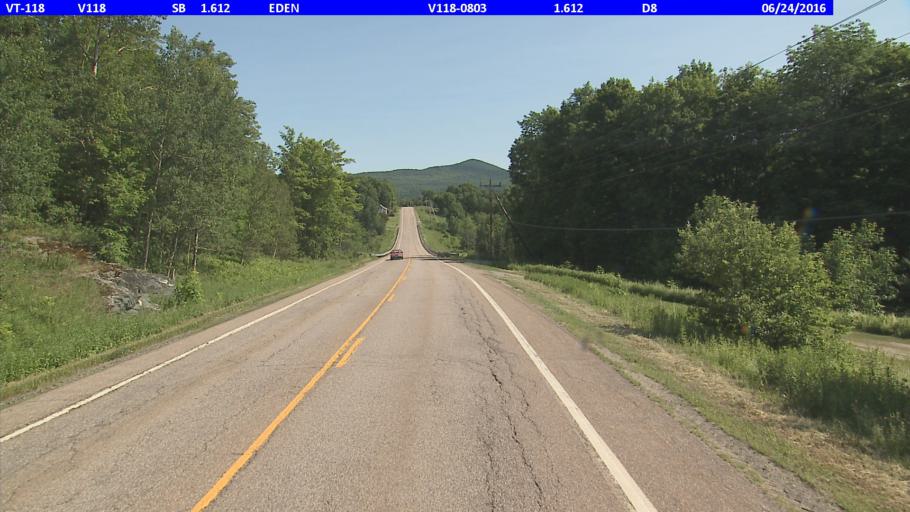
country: US
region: Vermont
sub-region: Lamoille County
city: Hyde Park
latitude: 44.7274
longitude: -72.5619
